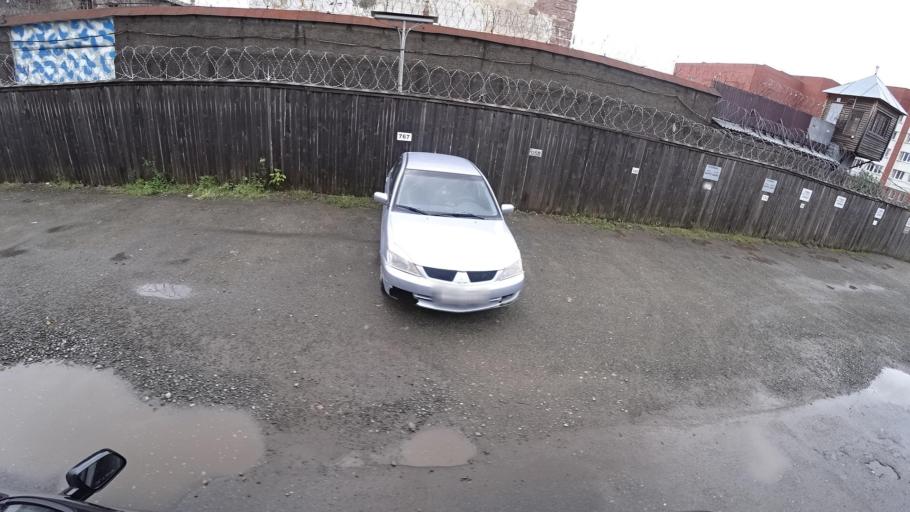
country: RU
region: Sverdlovsk
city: Kamyshlov
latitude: 56.8493
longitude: 62.7006
